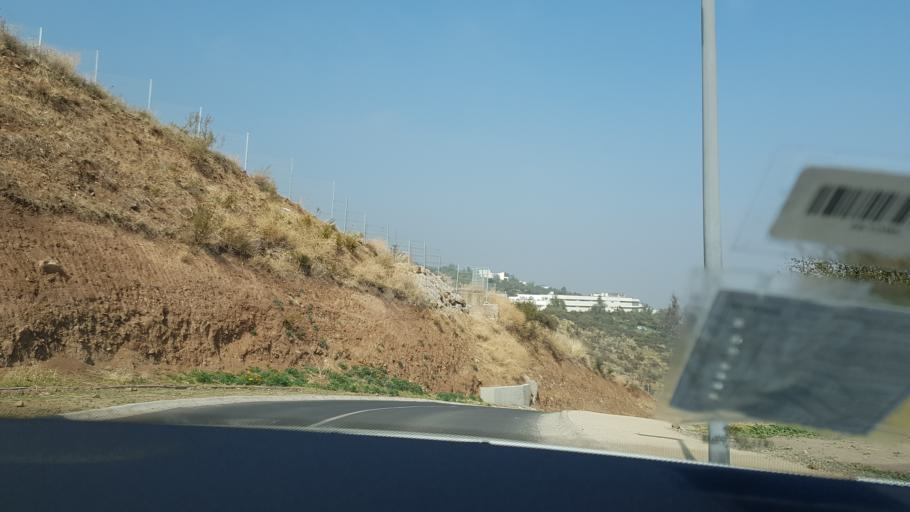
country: CL
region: Santiago Metropolitan
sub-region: Provincia de Santiago
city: Villa Presidente Frei, Nunoa, Santiago, Chile
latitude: -33.4799
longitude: -70.5167
